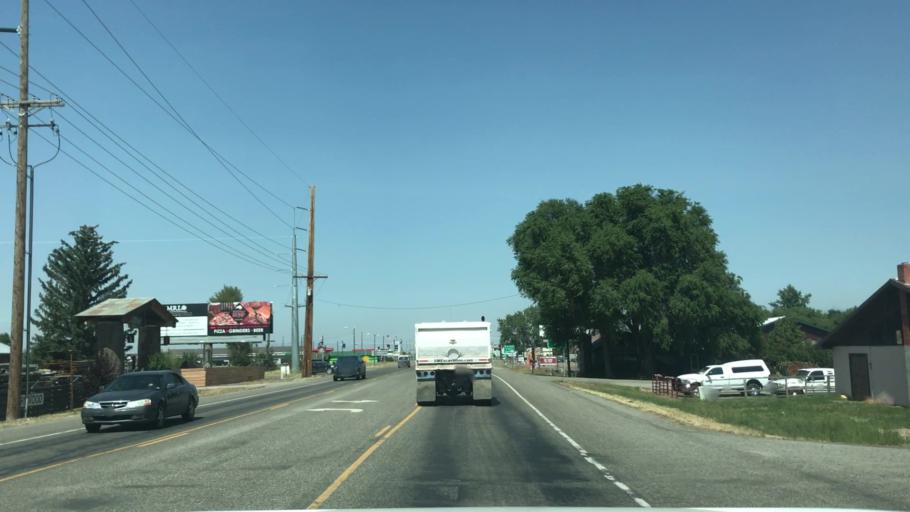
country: US
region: Montana
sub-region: Gallatin County
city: Four Corners
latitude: 45.6666
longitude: -111.1856
